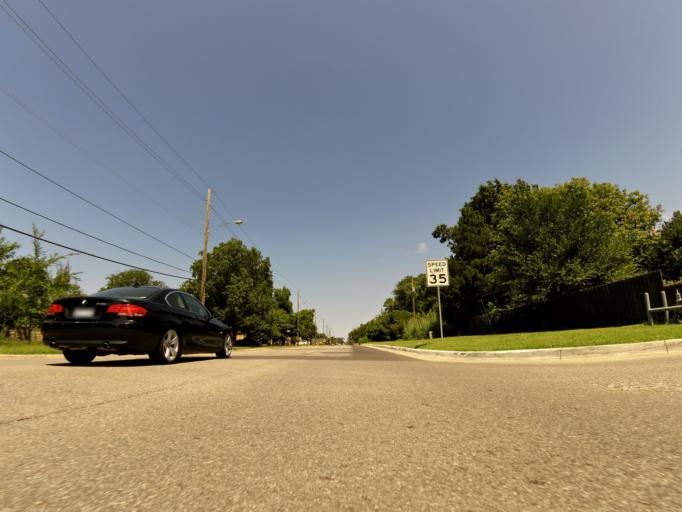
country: US
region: Kansas
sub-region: Sedgwick County
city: Bellaire
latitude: 37.6906
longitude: -97.2621
